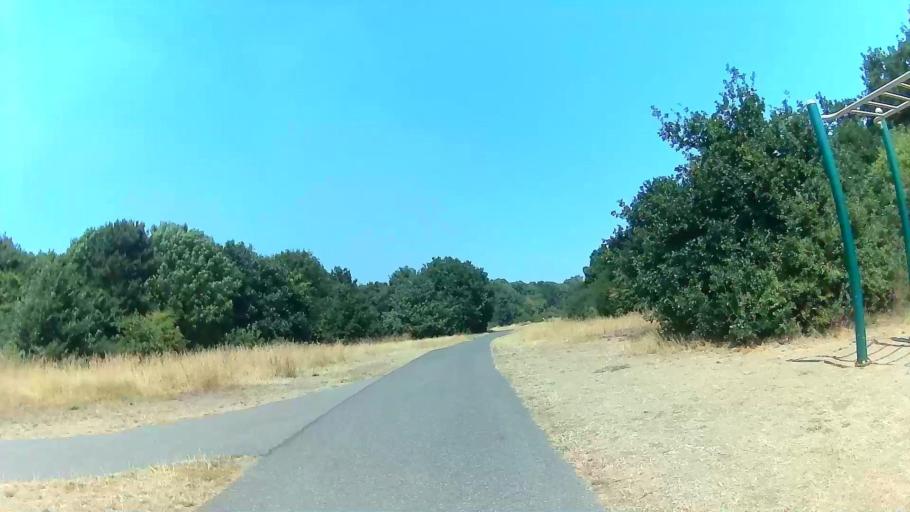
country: GB
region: England
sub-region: Greater London
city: Elm Park
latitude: 51.5388
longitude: 0.2139
